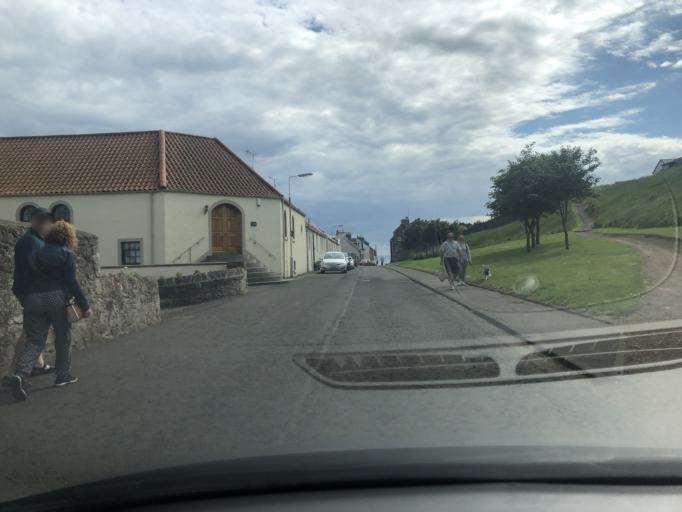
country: GB
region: Scotland
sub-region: Fife
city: Anstruther
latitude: 56.2275
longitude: -2.6814
